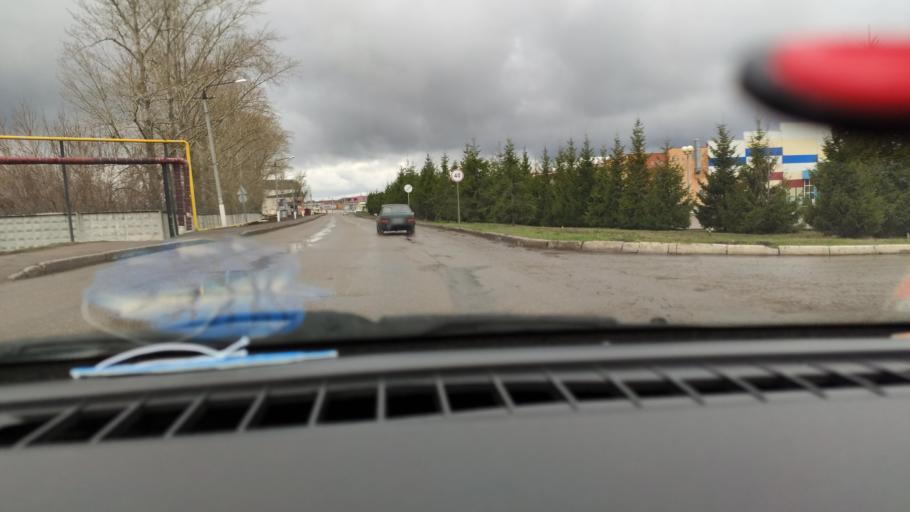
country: RU
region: Tatarstan
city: Nurlat
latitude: 54.4254
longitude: 50.7960
